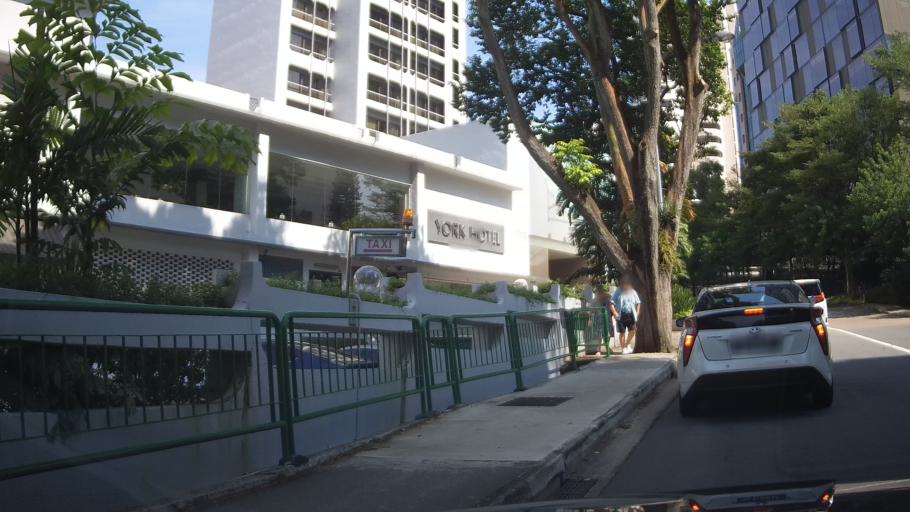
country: SG
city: Singapore
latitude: 1.3069
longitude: 103.8358
